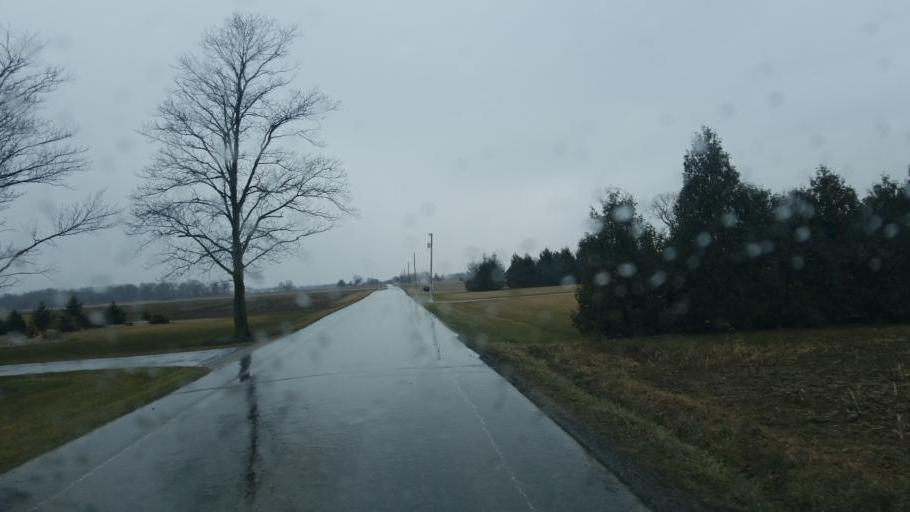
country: US
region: Indiana
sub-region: Adams County
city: Berne
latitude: 40.6722
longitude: -84.9602
